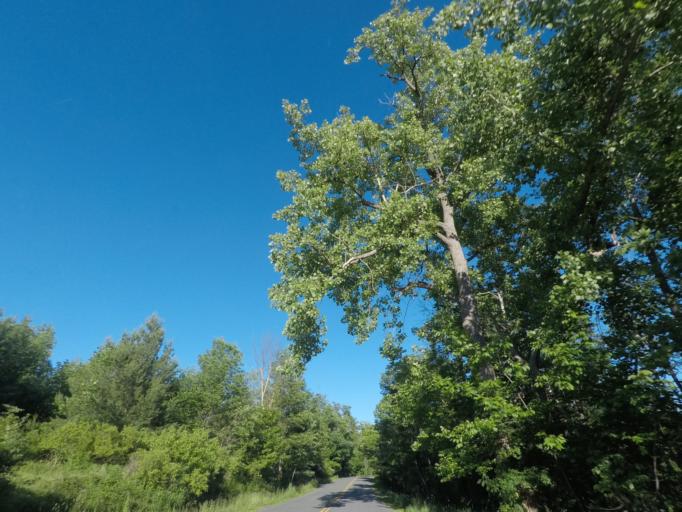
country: US
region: New York
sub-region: Rensselaer County
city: Averill Park
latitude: 42.5824
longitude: -73.5523
